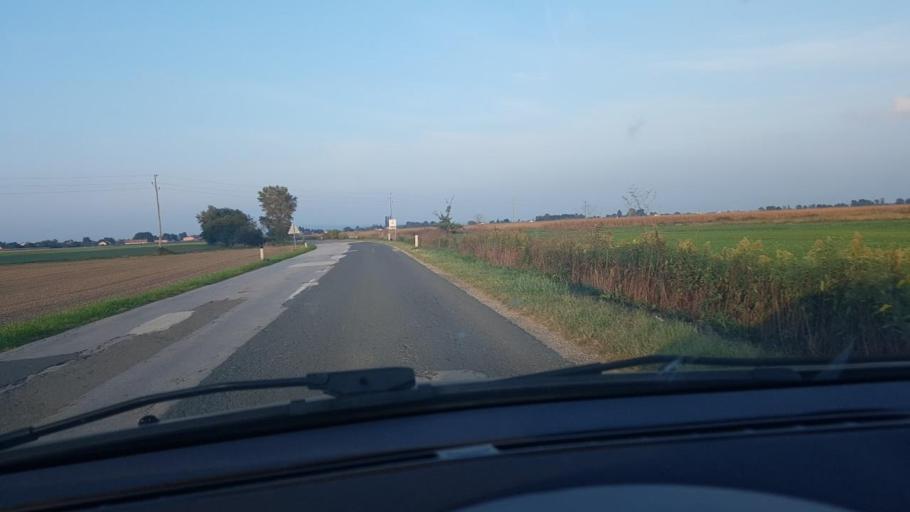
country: SI
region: Slovenska Bistrica
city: Pragersko
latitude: 46.3948
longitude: 15.6914
